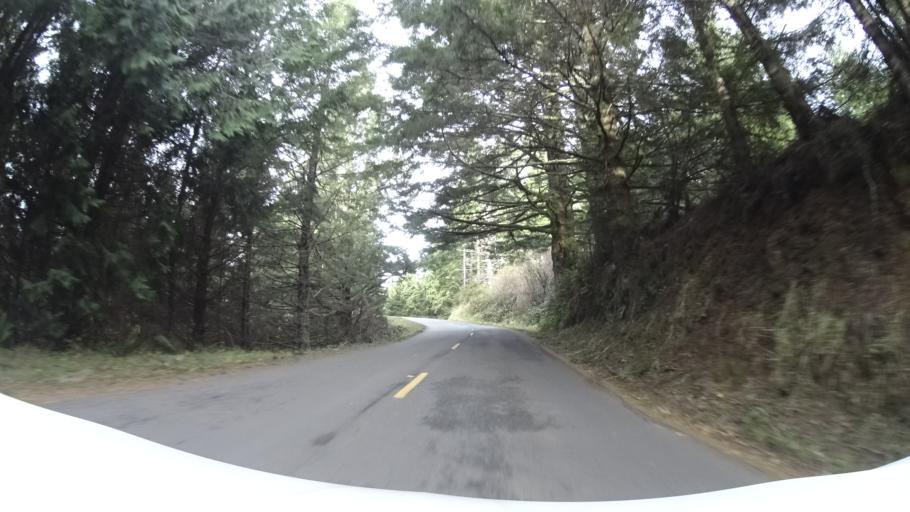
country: US
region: California
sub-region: Humboldt County
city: Ferndale
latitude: 40.5152
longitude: -124.2705
